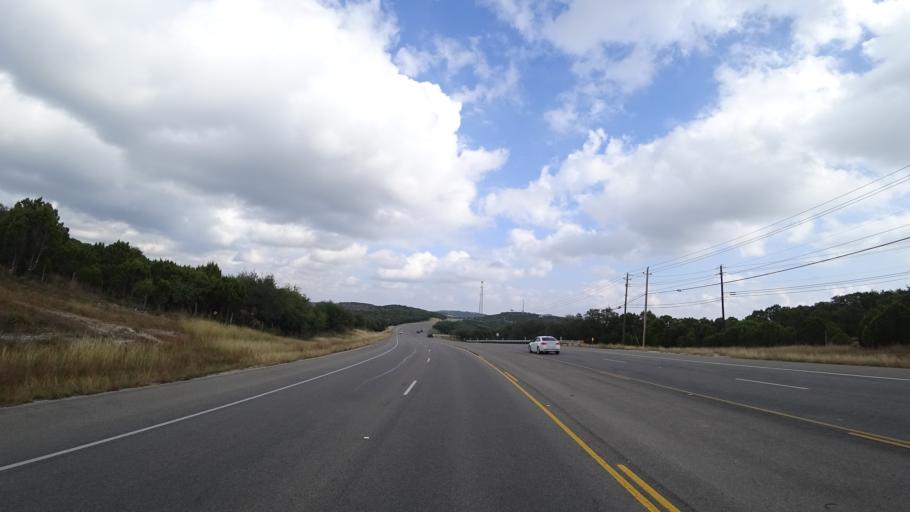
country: US
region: Texas
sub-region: Travis County
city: Barton Creek
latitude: 30.3093
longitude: -97.8889
